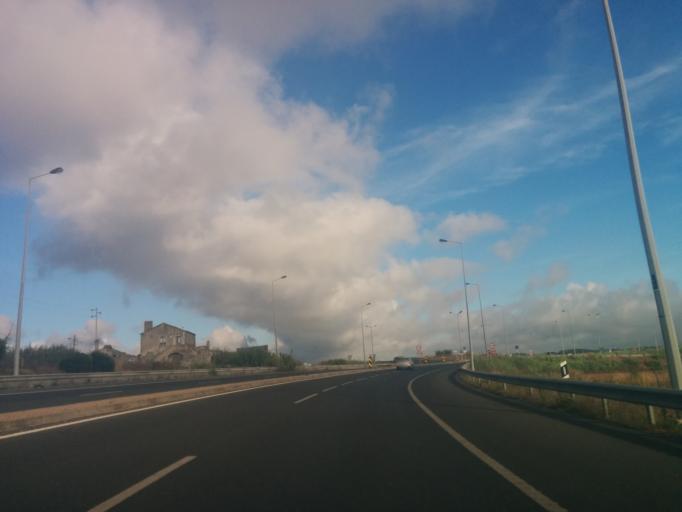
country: PT
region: Leiria
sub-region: Peniche
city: Atouguia da Baleia
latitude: 39.3468
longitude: -9.3431
